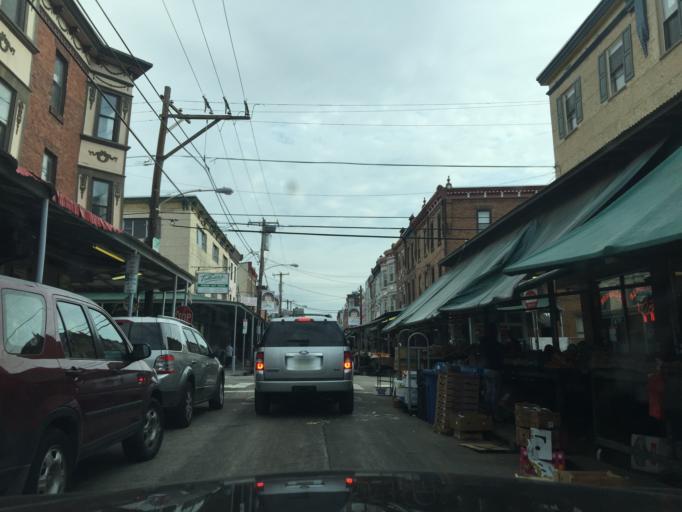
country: US
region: Pennsylvania
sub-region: Philadelphia County
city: Philadelphia
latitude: 39.9374
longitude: -75.1582
